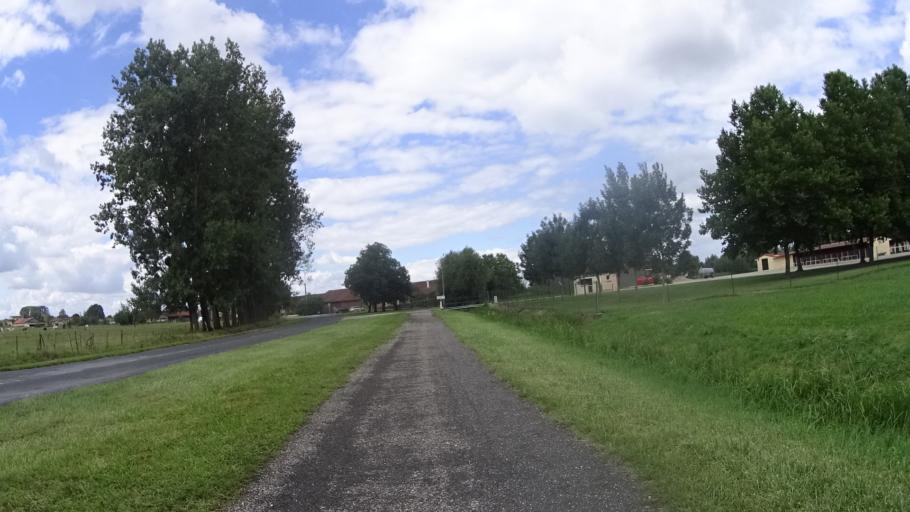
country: FR
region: Champagne-Ardenne
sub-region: Departement de la Haute-Marne
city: Montier-en-Der
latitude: 48.4772
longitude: 4.7605
